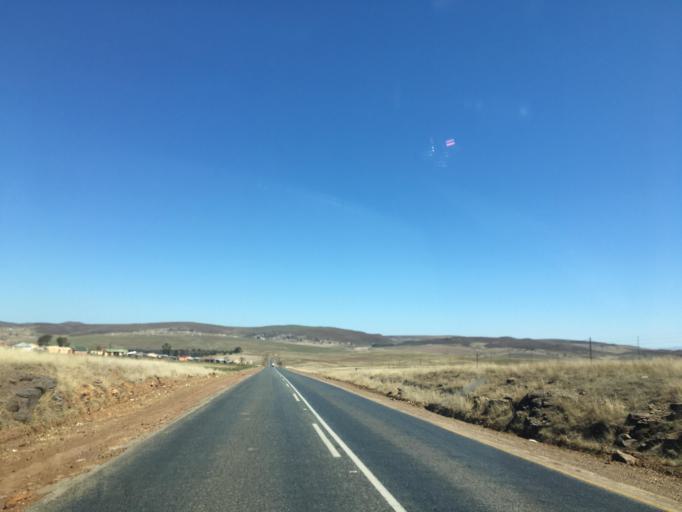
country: ZA
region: Eastern Cape
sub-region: Chris Hani District Municipality
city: Cofimvaba
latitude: -31.9594
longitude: 27.8238
